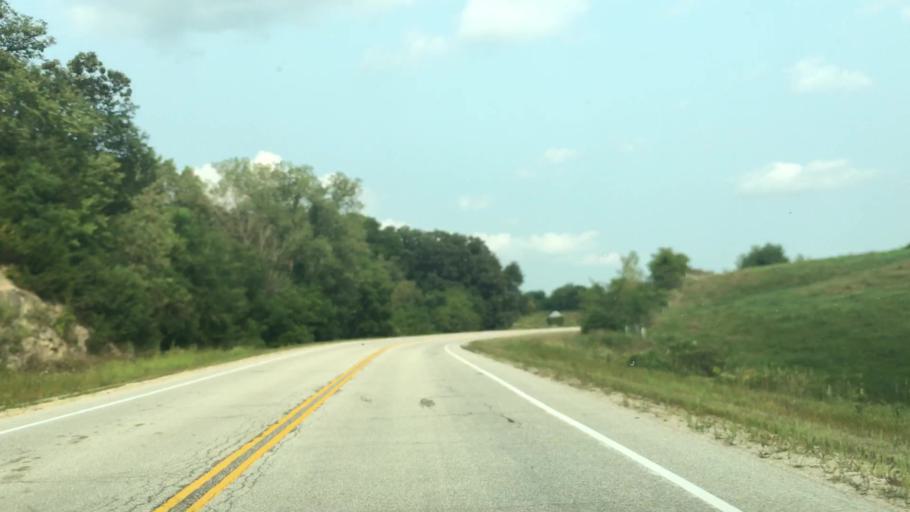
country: US
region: Minnesota
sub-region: Fillmore County
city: Preston
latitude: 43.6973
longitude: -91.9571
